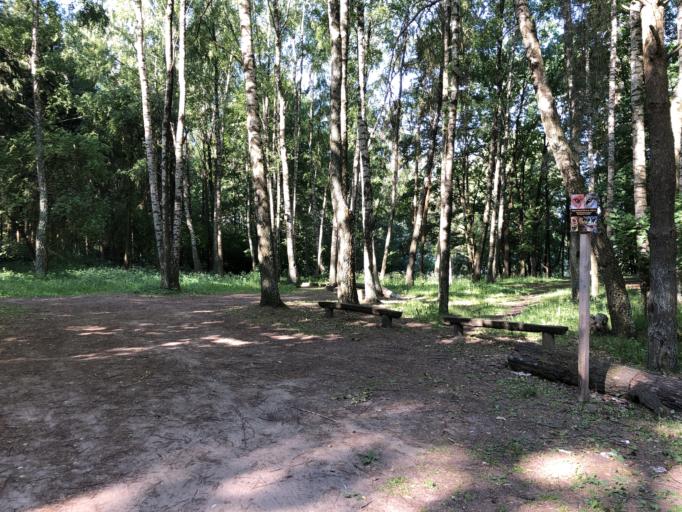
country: LT
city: Ramuciai
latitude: 54.8762
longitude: 24.0516
